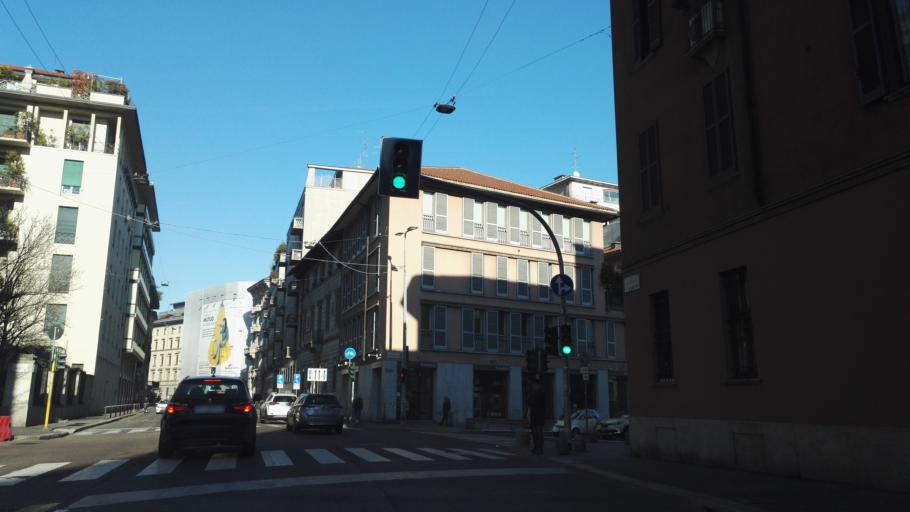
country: IT
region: Lombardy
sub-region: Citta metropolitana di Milano
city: Milano
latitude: 45.4655
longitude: 9.2005
